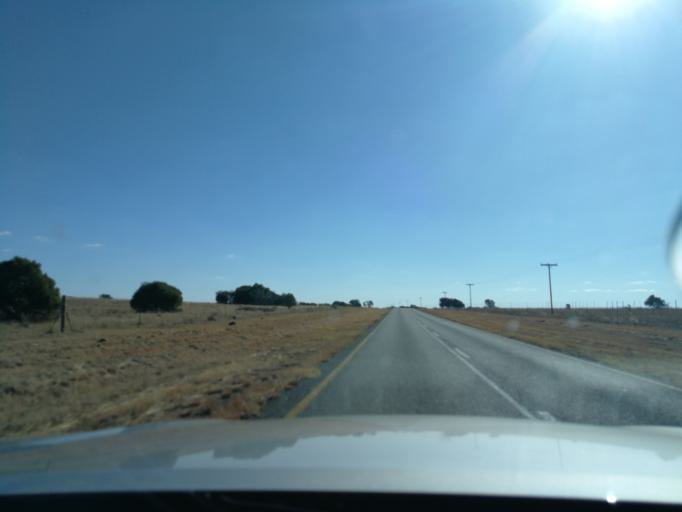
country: ZA
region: North-West
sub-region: Ngaka Modiri Molema District Municipality
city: Zeerust
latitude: -25.7811
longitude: 26.0062
